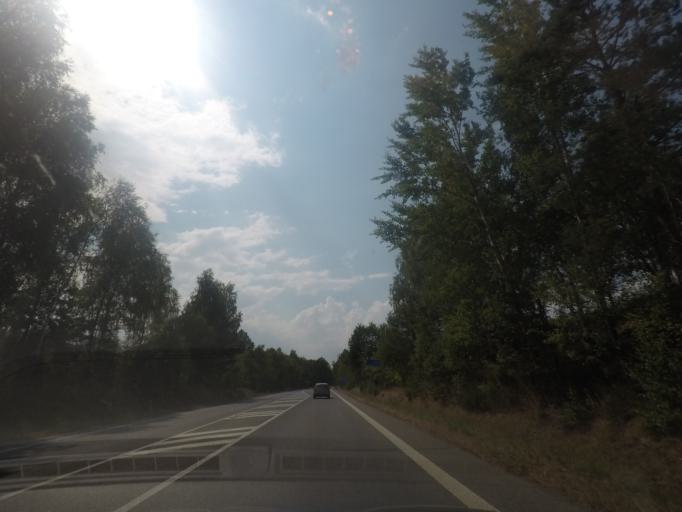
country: CZ
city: Brniste
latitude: 50.7719
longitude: 14.6851
